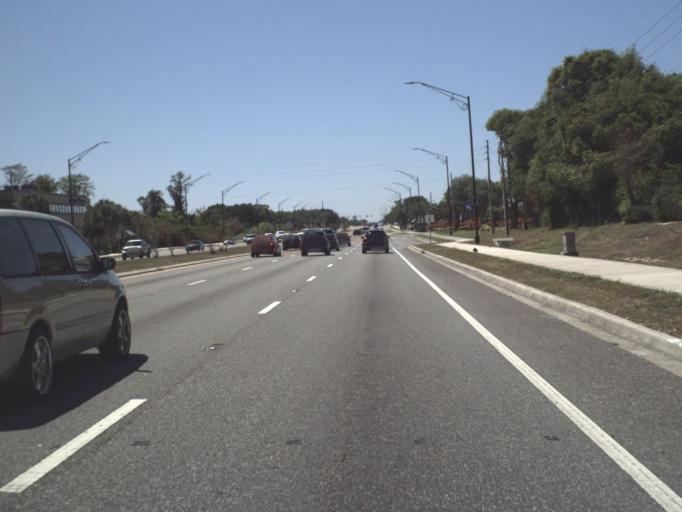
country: US
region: Florida
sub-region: Orange County
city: Conway
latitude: 28.5109
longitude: -81.3104
